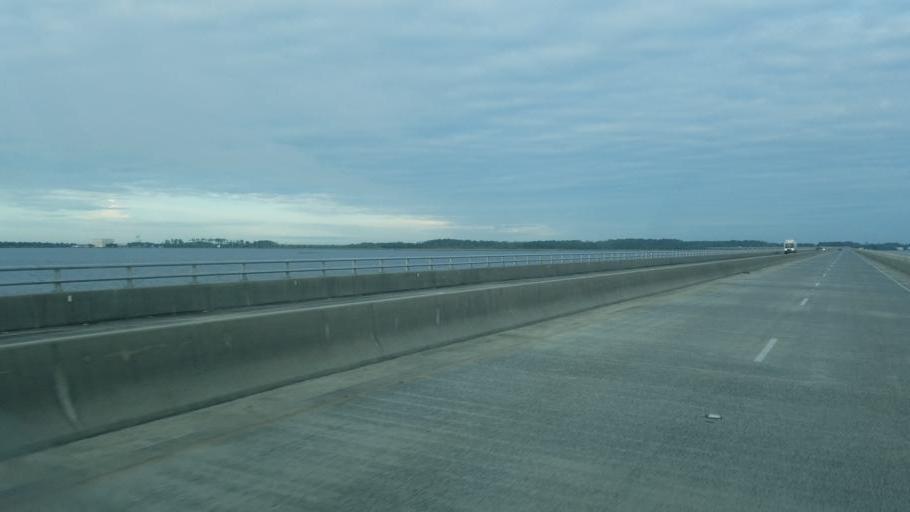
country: US
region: North Carolina
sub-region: Dare County
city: Manteo
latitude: 35.8874
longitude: -75.7358
